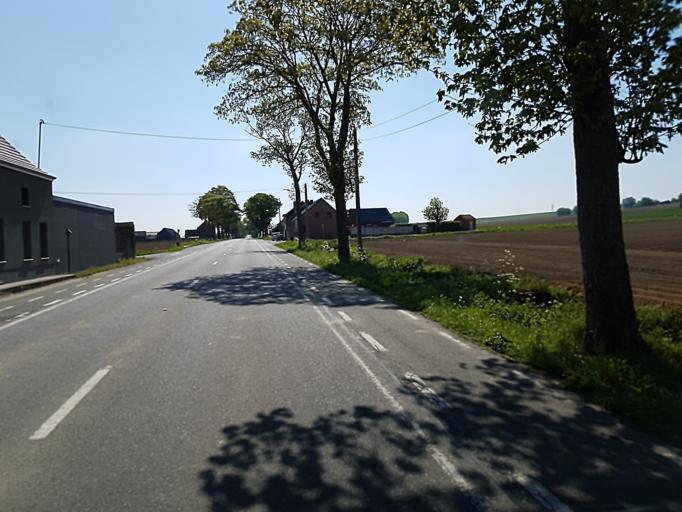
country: BE
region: Wallonia
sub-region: Province du Hainaut
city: Chievres
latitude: 50.6040
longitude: 3.8132
